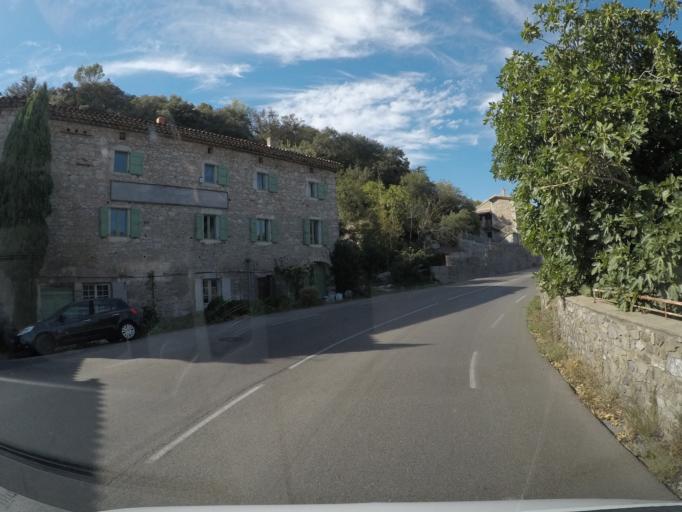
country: FR
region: Languedoc-Roussillon
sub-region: Departement du Gard
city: Boisset-et-Gaujac
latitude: 44.0371
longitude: 4.0009
